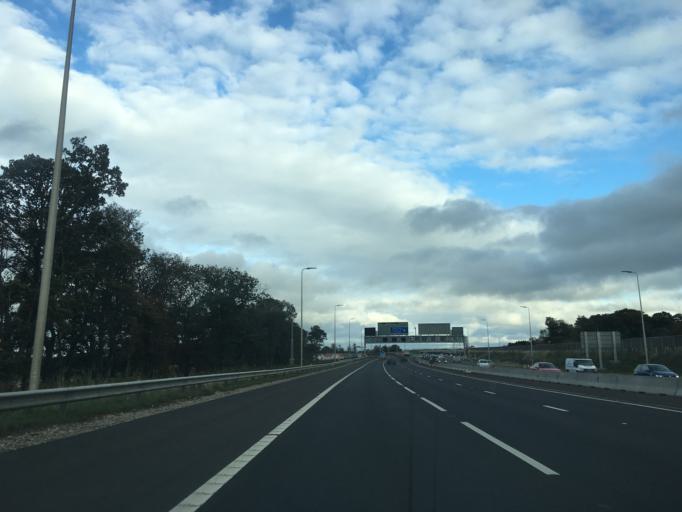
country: GB
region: Scotland
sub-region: Edinburgh
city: Queensferry
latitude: 55.9809
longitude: -3.4084
